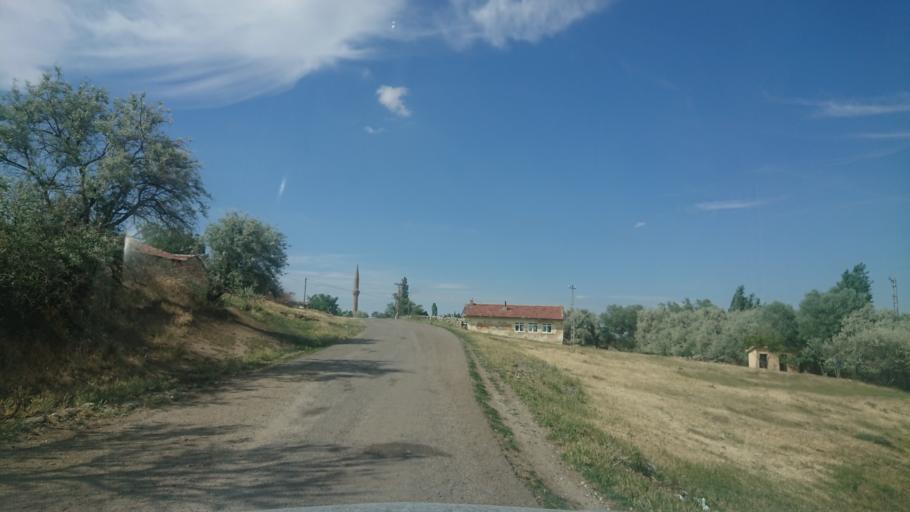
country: TR
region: Aksaray
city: Ortakoy
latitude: 38.8202
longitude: 34.0043
